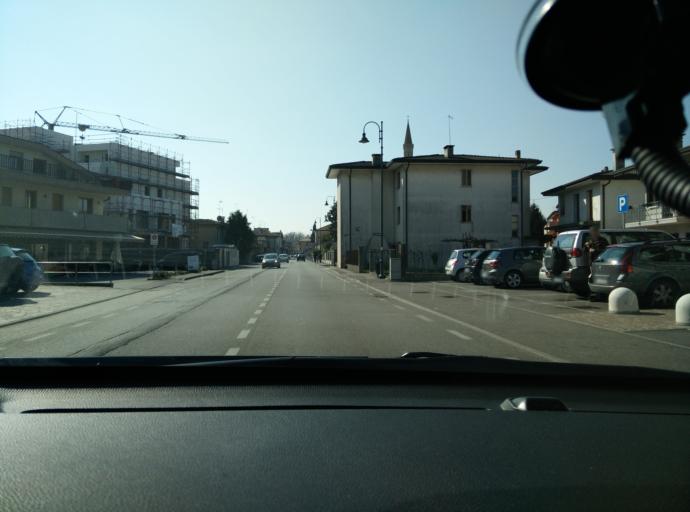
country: IT
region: Veneto
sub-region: Provincia di Venezia
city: Noventa di Piave
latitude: 45.6640
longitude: 12.5319
